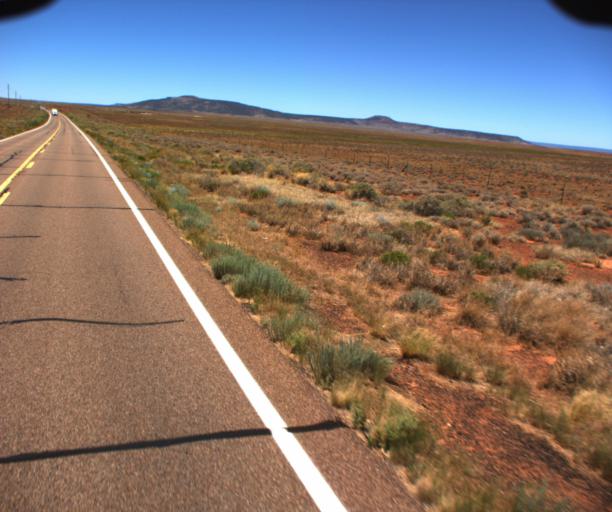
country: US
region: Arizona
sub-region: Coconino County
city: LeChee
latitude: 34.9165
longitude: -110.8270
